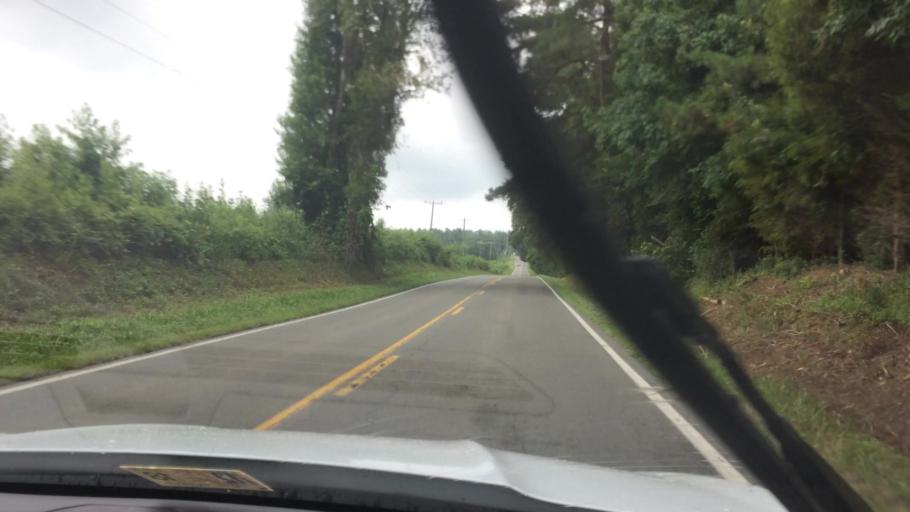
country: US
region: Virginia
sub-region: Charles City County
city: Charles City
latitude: 37.4207
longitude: -77.0414
